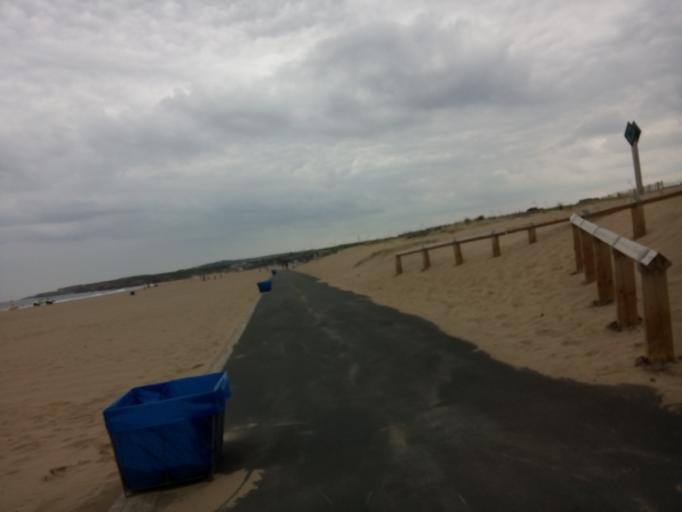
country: GB
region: England
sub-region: South Tyneside
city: South Shields
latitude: 55.0000
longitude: -1.4127
